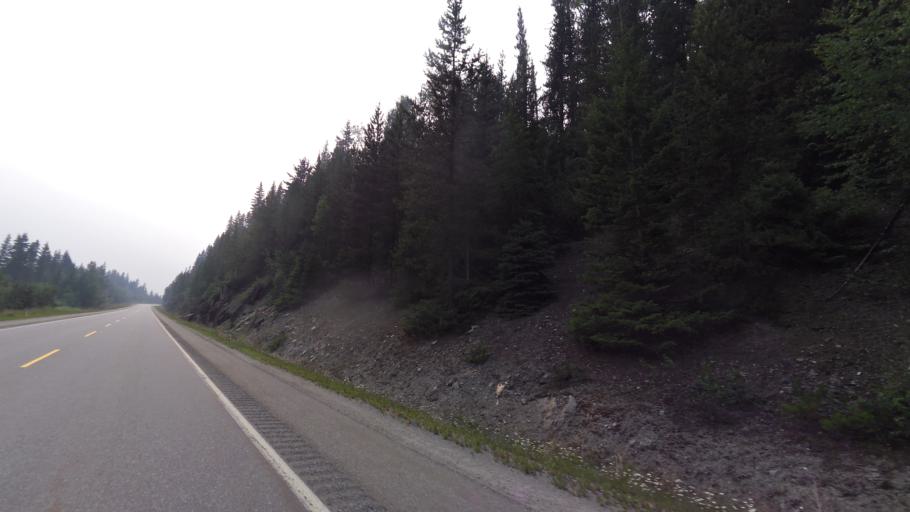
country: CA
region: Alberta
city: Grande Cache
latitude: 53.0200
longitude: -119.1119
